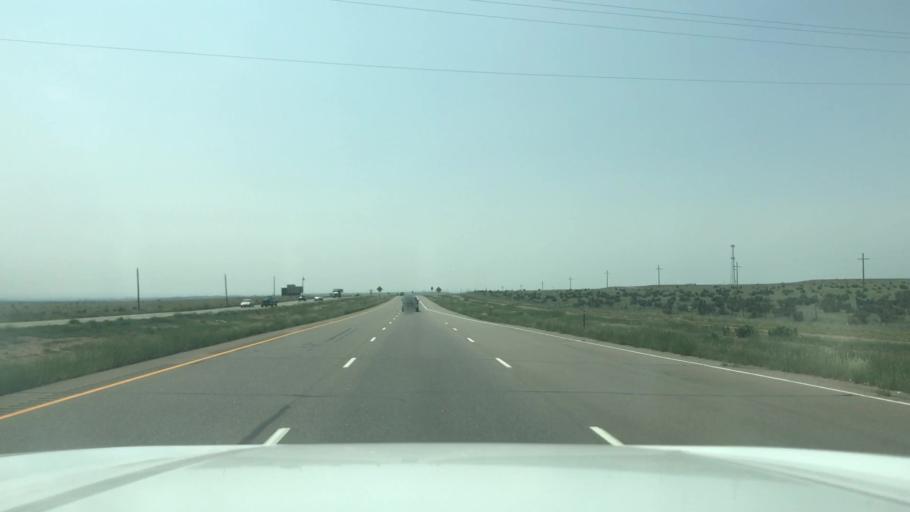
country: US
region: Colorado
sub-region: Pueblo County
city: Pueblo West
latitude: 38.3999
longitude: -104.6177
